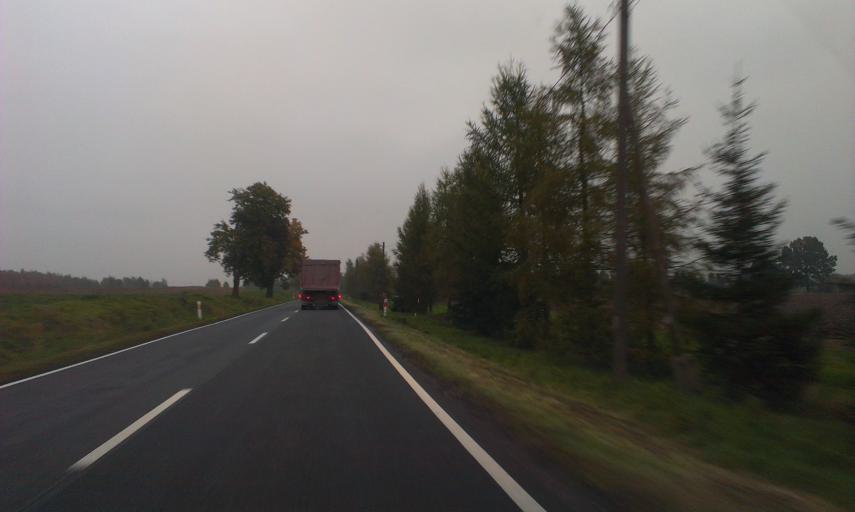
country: PL
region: Kujawsko-Pomorskie
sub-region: Powiat sepolenski
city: Sosno
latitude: 53.4383
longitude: 17.6190
